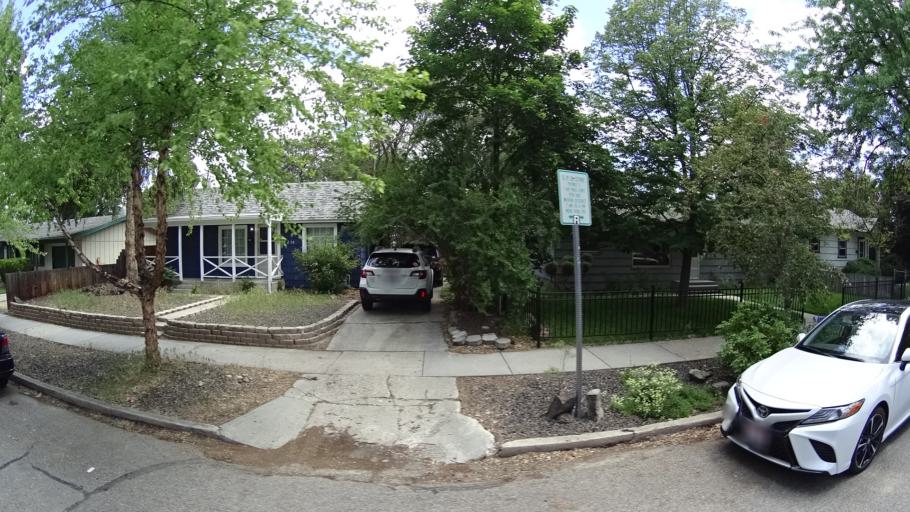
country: US
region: Idaho
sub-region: Ada County
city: Boise
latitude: 43.5977
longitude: -116.1986
